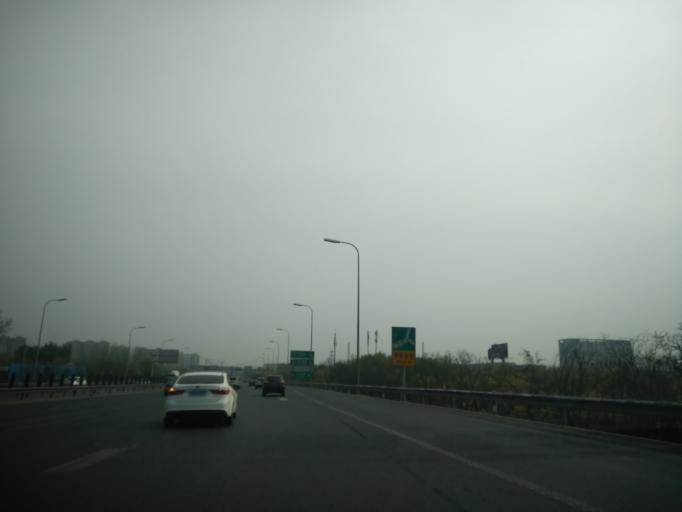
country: CN
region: Beijing
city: Dongfeng
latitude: 39.8639
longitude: 116.5420
